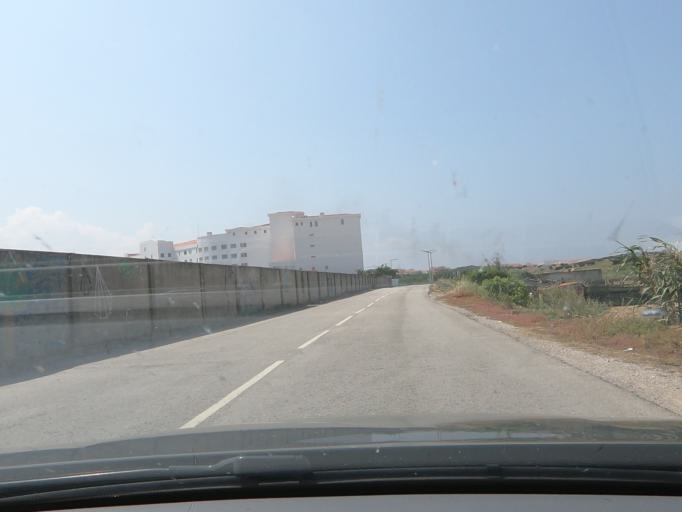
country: PT
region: Leiria
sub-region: Peniche
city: Atouguia da Baleia
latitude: 39.3370
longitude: -9.3542
